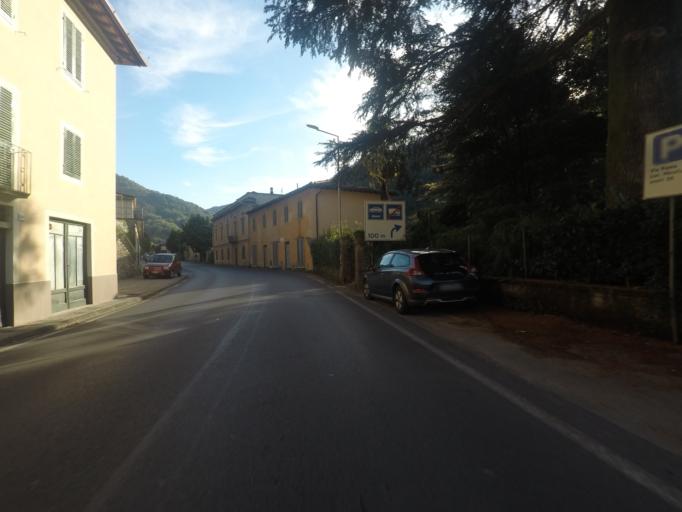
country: IT
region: Tuscany
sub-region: Provincia di Lucca
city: Bagni di Lucca
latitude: 44.0067
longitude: 10.5870
